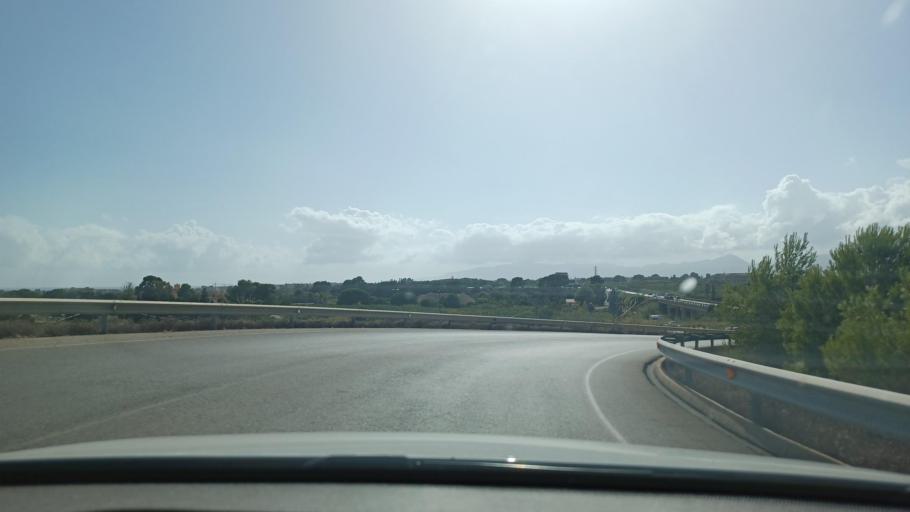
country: ES
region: Catalonia
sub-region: Provincia de Tarragona
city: Cambrils
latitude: 41.0830
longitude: 1.0777
